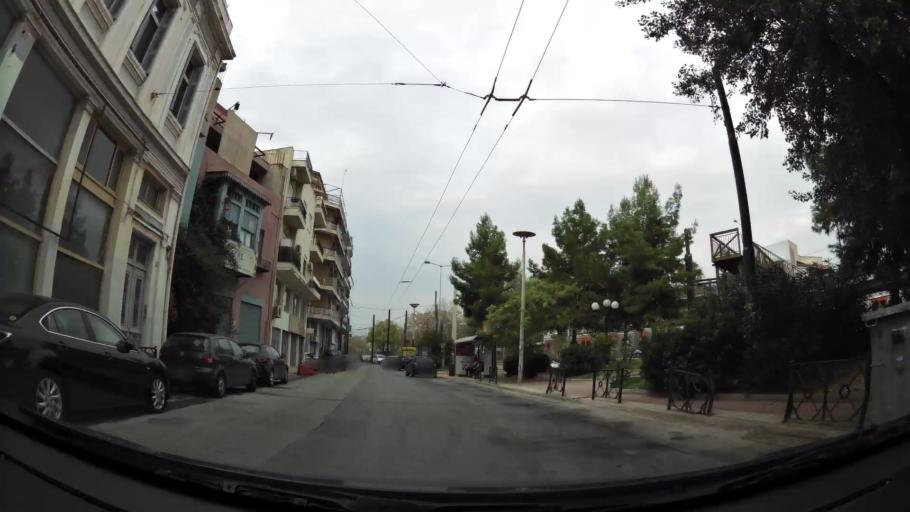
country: GR
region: Attica
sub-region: Nomarchia Athinas
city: Moskhaton
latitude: 37.9444
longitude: 23.6616
